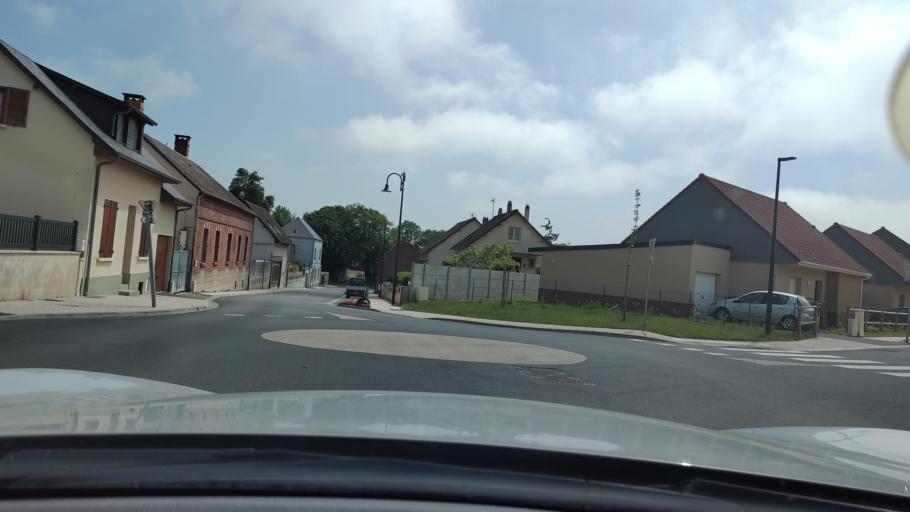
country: FR
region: Picardie
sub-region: Departement de la Somme
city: Ault
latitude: 50.0703
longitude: 1.4603
